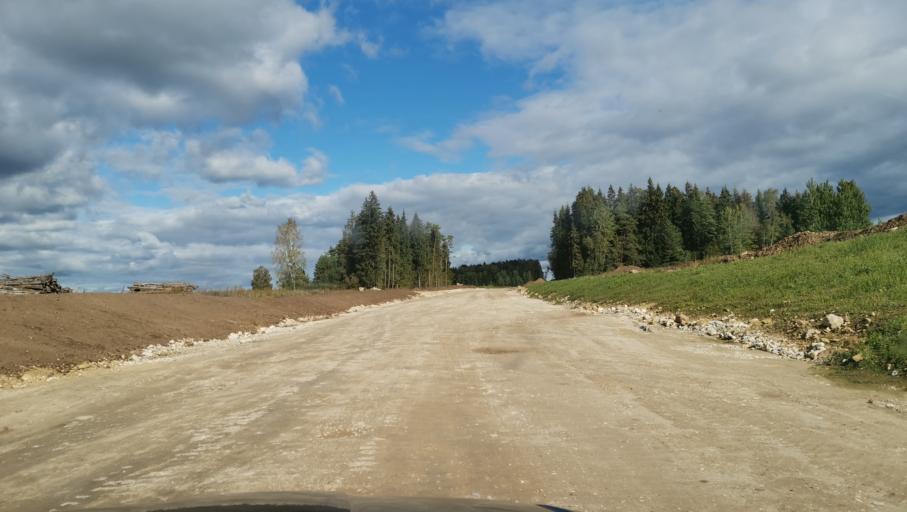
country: EE
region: Harju
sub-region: Nissi vald
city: Riisipere
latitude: 59.1346
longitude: 24.4823
